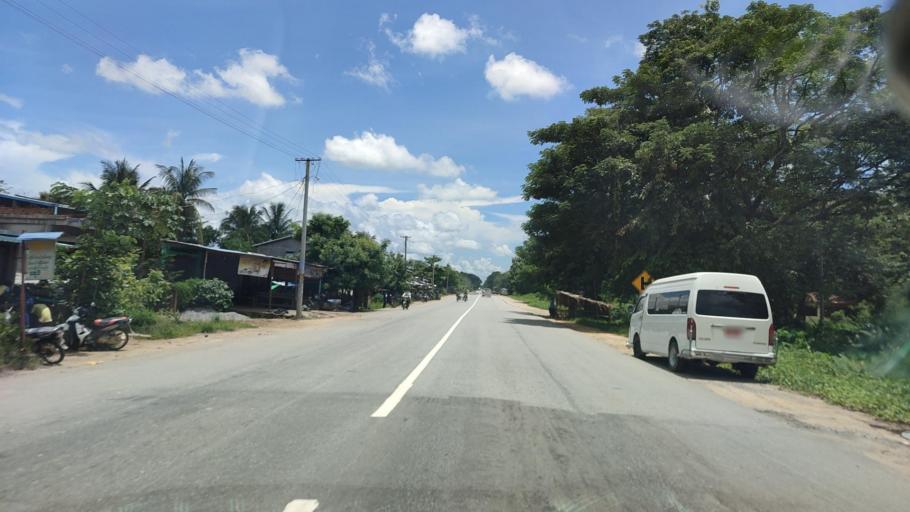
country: MM
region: Bago
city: Pyu
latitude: 18.4139
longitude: 96.4567
